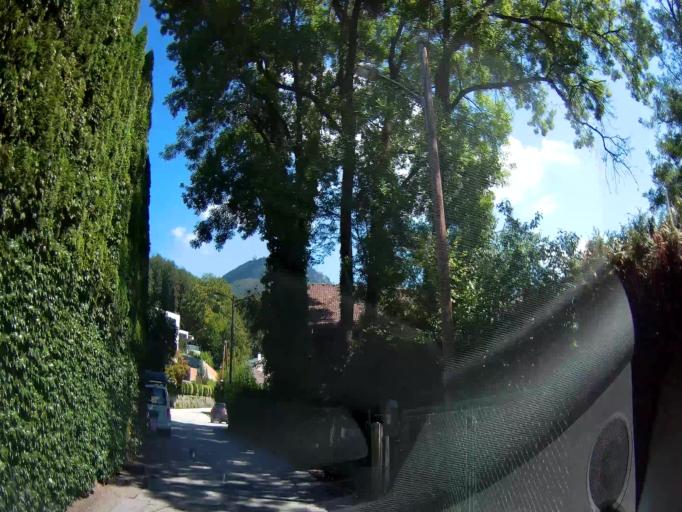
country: AT
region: Salzburg
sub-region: Salzburg Stadt
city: Salzburg
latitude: 47.8062
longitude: 13.0772
